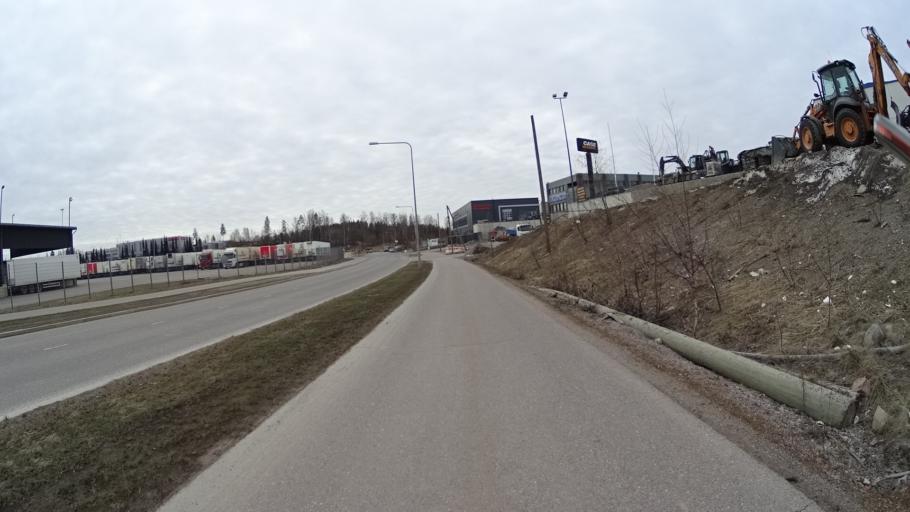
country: FI
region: Uusimaa
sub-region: Helsinki
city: Teekkarikylae
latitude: 60.3006
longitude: 24.9050
